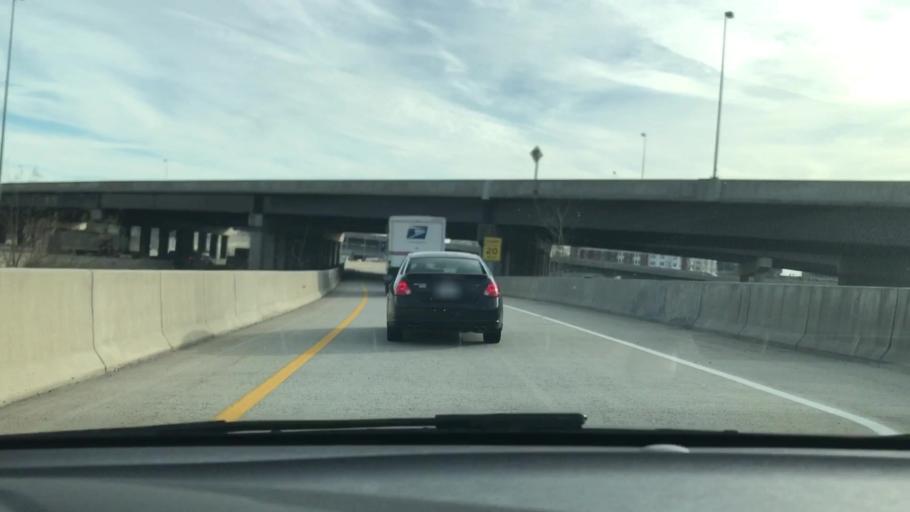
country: US
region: Virginia
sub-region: Fairfax County
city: Belle Haven
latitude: 38.7934
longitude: -77.0561
